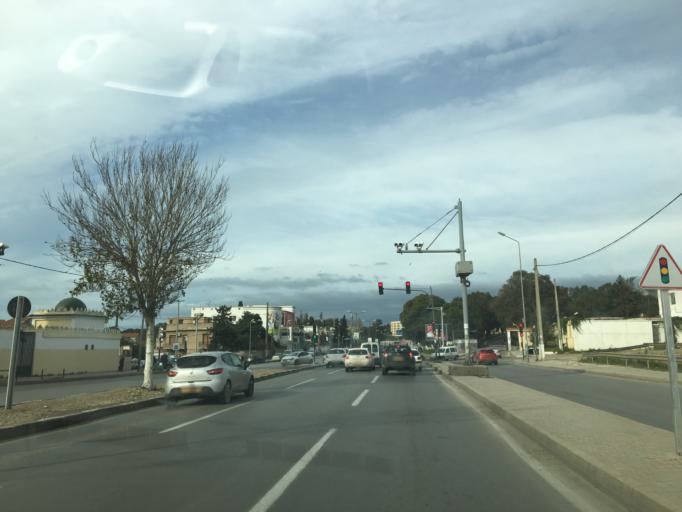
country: DZ
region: Alger
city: Algiers
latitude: 36.7705
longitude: 3.0041
